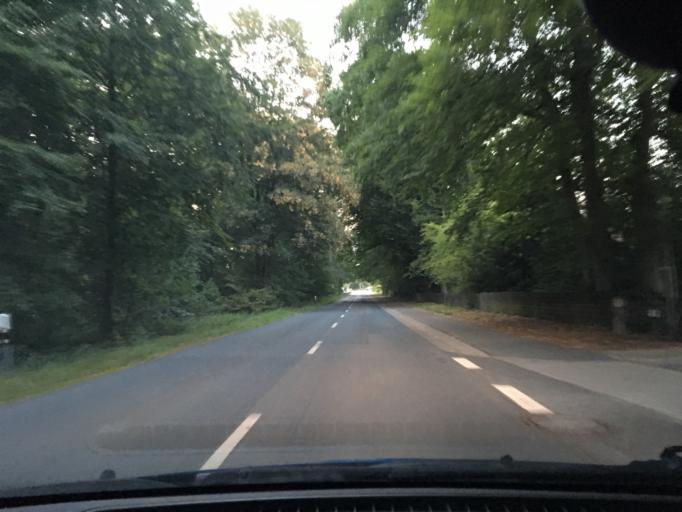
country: DE
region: Lower Saxony
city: Embsen
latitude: 53.1710
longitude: 10.3449
